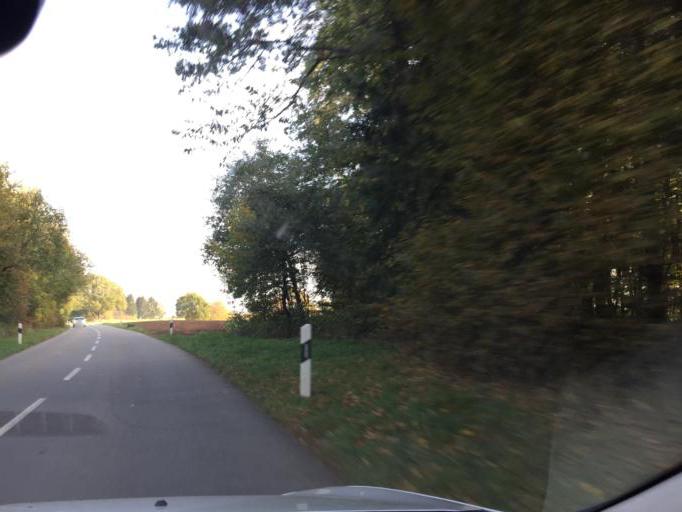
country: LU
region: Luxembourg
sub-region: Canton de Luxembourg
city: Contern
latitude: 49.5719
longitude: 6.2170
